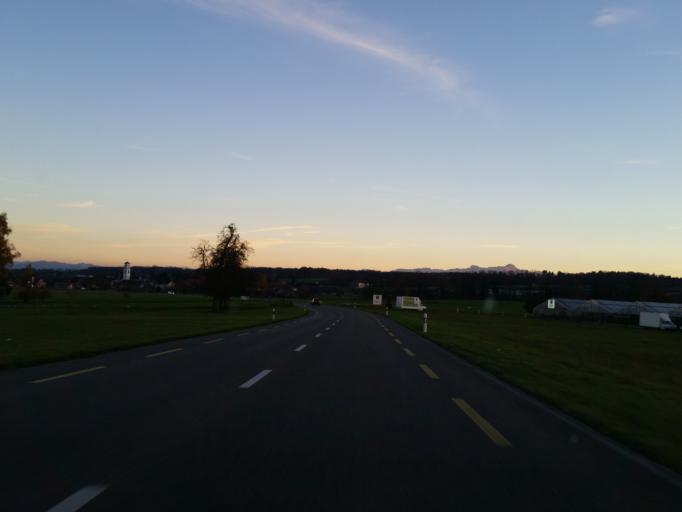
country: CH
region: Thurgau
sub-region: Kreuzlingen District
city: Guttingen
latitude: 47.6107
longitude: 9.2777
